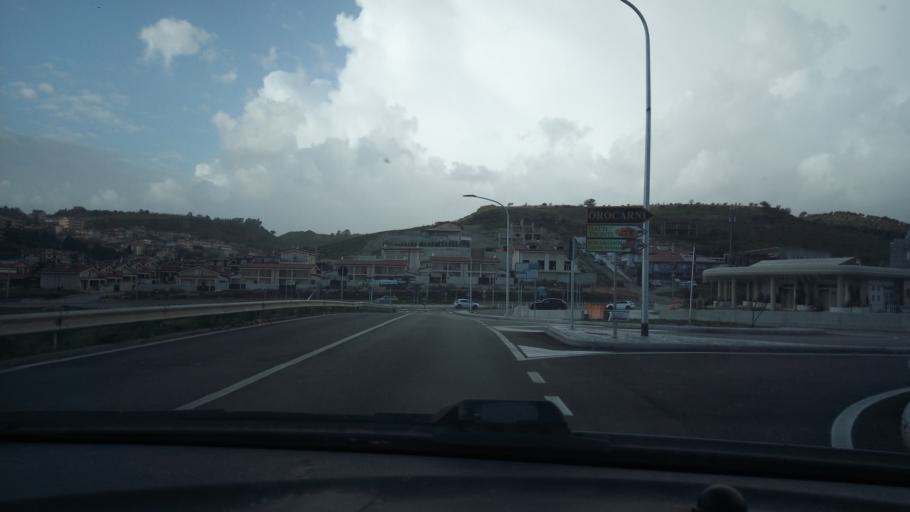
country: IT
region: Calabria
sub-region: Provincia di Catanzaro
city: Barone
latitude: 38.8344
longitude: 16.6373
